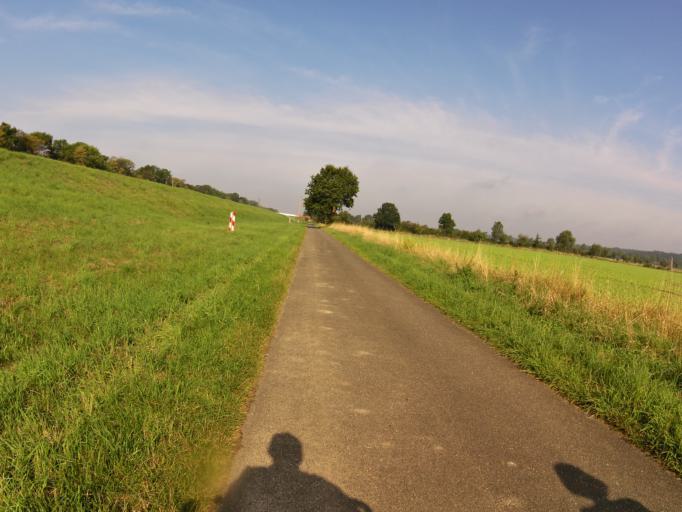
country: DE
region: Lower Saxony
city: Langwedel
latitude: 52.9660
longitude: 9.1656
